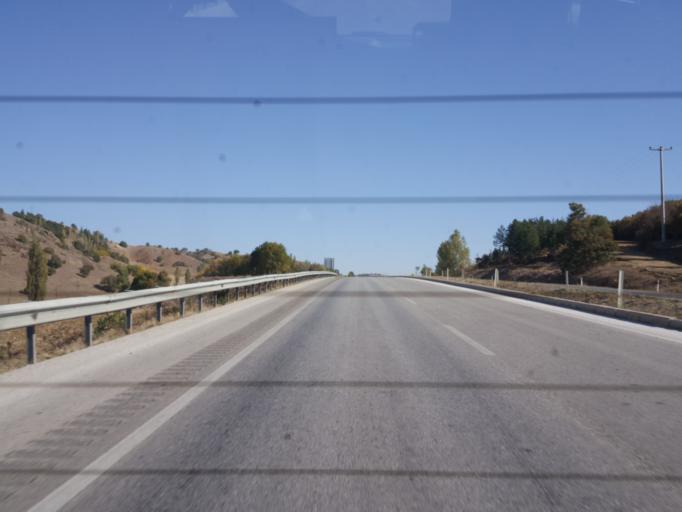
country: TR
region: Corum
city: Alaca
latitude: 40.2782
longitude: 34.6437
